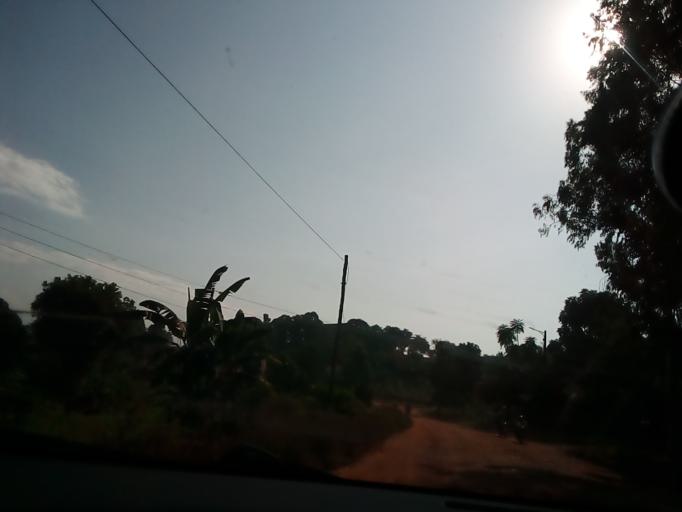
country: UG
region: Central Region
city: Masaka
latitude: -0.3340
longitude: 31.7343
